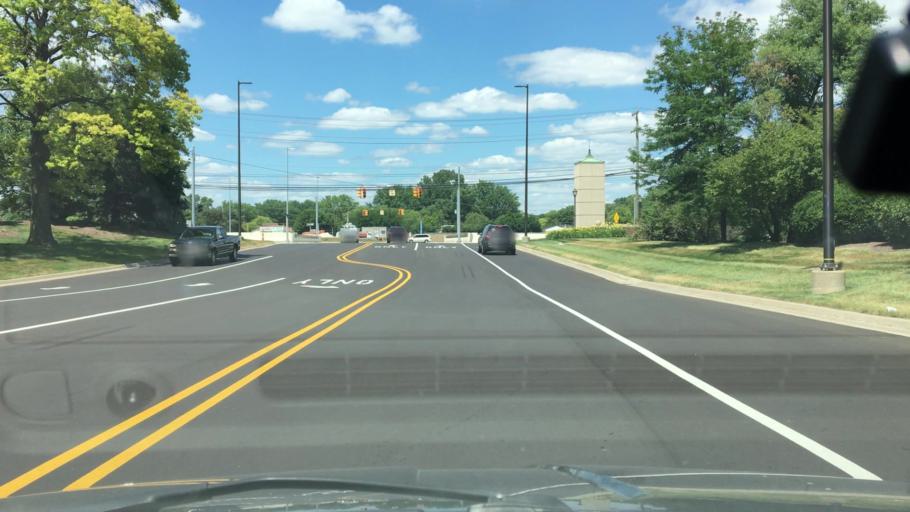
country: US
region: Michigan
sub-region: Wayne County
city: Livonia
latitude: 42.3825
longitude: -83.3266
